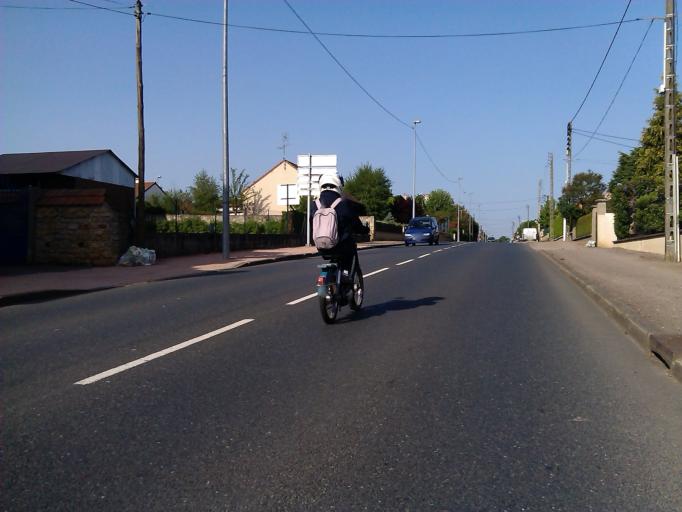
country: FR
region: Centre
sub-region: Departement de l'Indre
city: La Chatre
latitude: 46.5797
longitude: 1.9798
